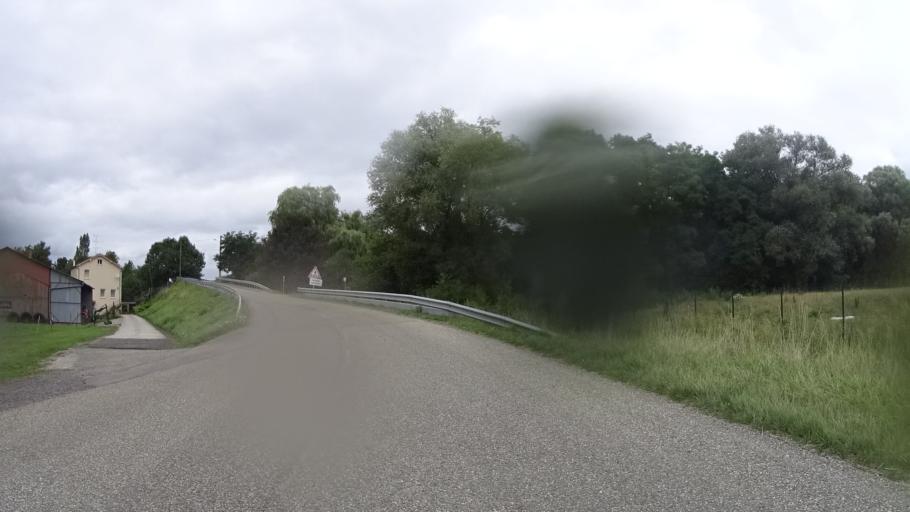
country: FR
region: Lorraine
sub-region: Departement de la Moselle
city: Dieuze
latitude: 48.6774
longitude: 6.7886
